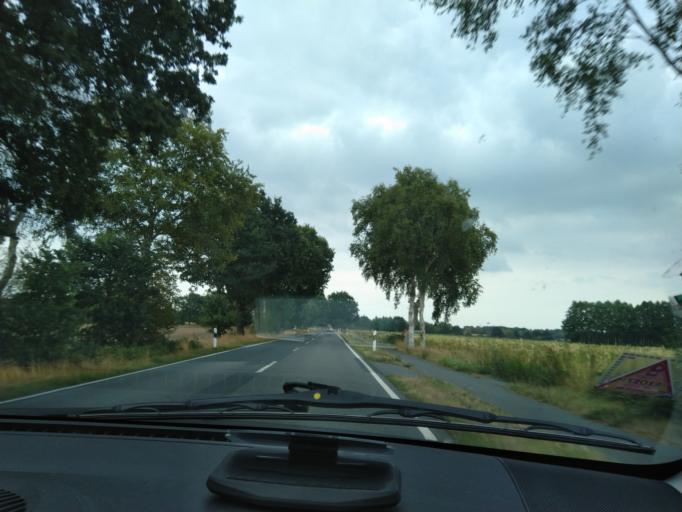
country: DE
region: Lower Saxony
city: Rhede
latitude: 53.0675
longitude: 7.2158
